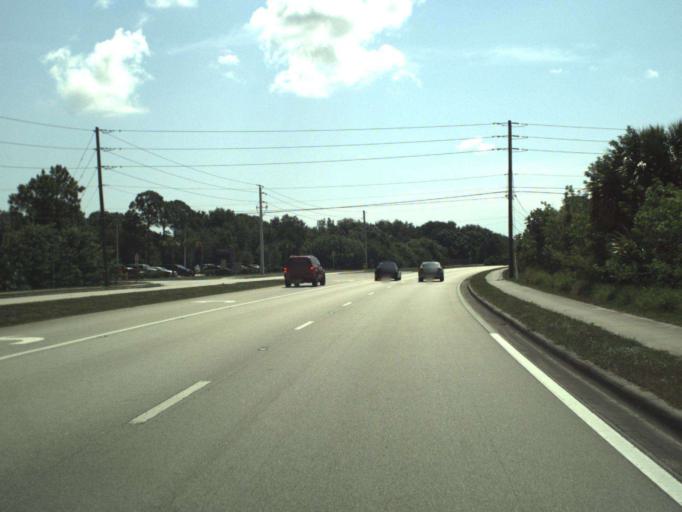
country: US
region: Florida
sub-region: Brevard County
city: June Park
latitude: 28.1278
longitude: -80.6845
